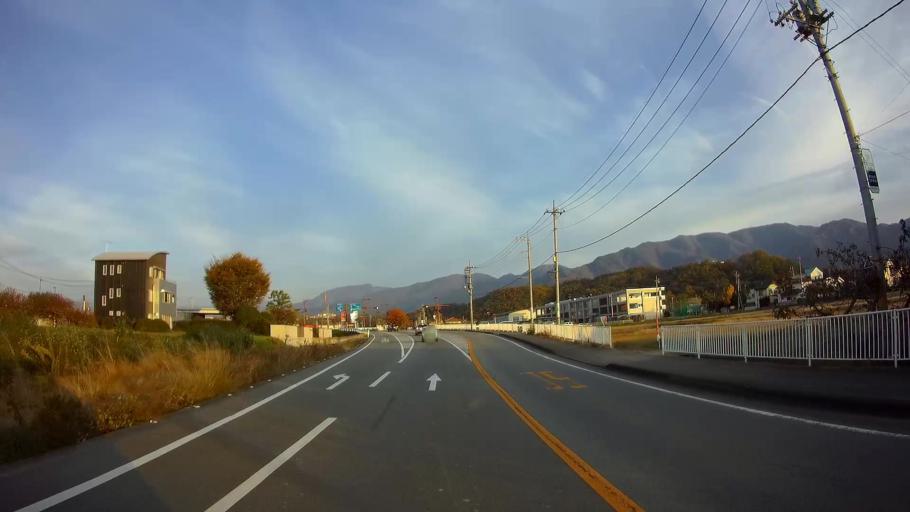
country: JP
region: Yamanashi
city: Kofu-shi
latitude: 35.5960
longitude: 138.5732
